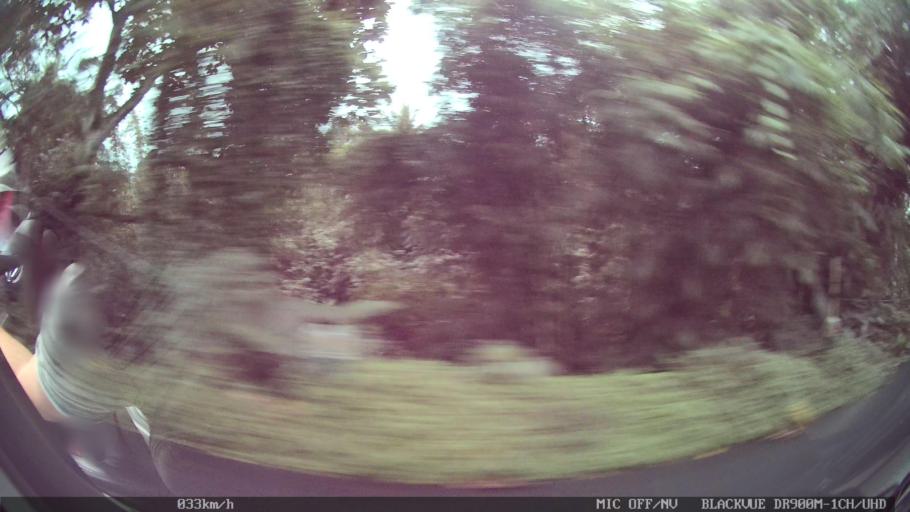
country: ID
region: Bali
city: Peneng
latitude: -8.3665
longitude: 115.1785
